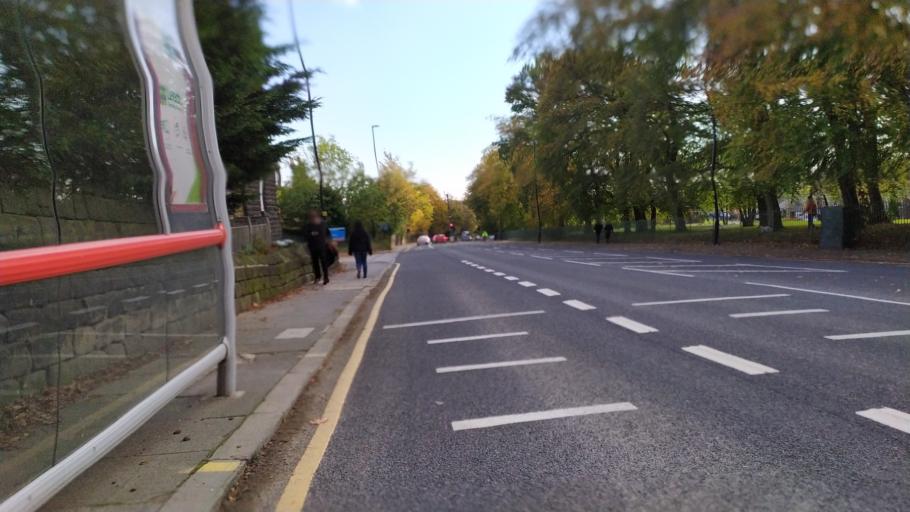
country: GB
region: England
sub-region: City and Borough of Leeds
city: Horsforth
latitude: 53.8321
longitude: -1.5898
